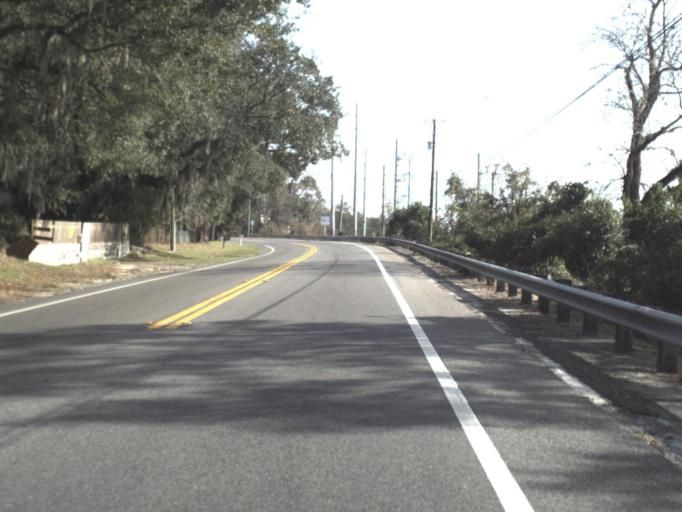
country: US
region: Florida
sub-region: Bay County
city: Parker
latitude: 30.1329
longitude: -85.6141
